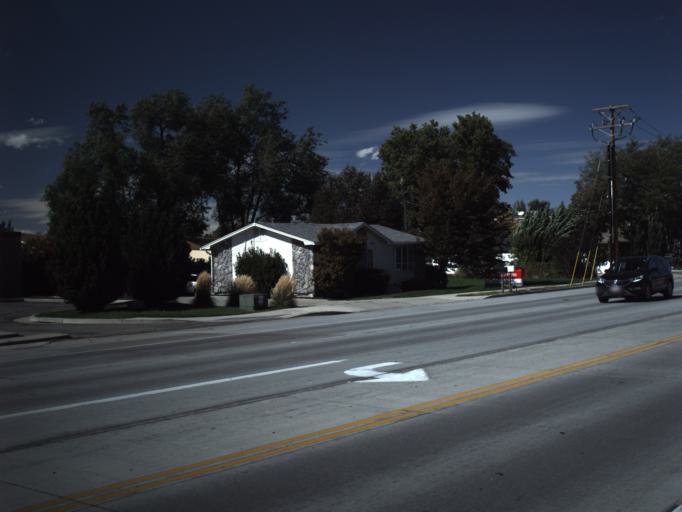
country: US
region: Utah
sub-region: Salt Lake County
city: South Jordan
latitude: 40.5662
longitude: -111.9386
